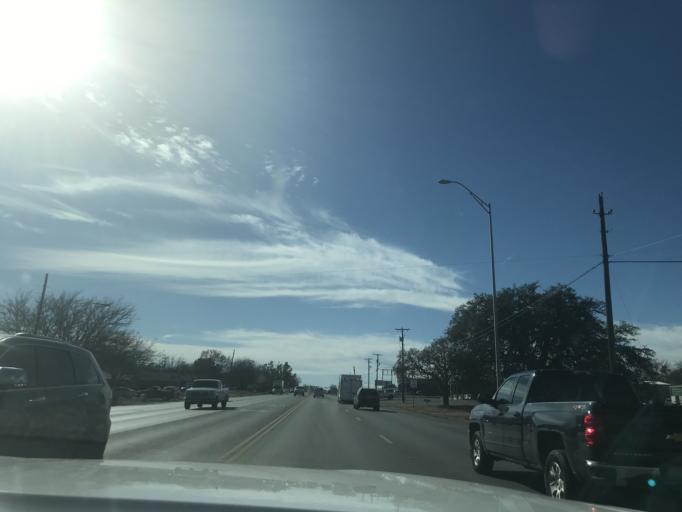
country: US
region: Texas
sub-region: Erath County
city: Stephenville
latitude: 32.2073
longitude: -98.2055
